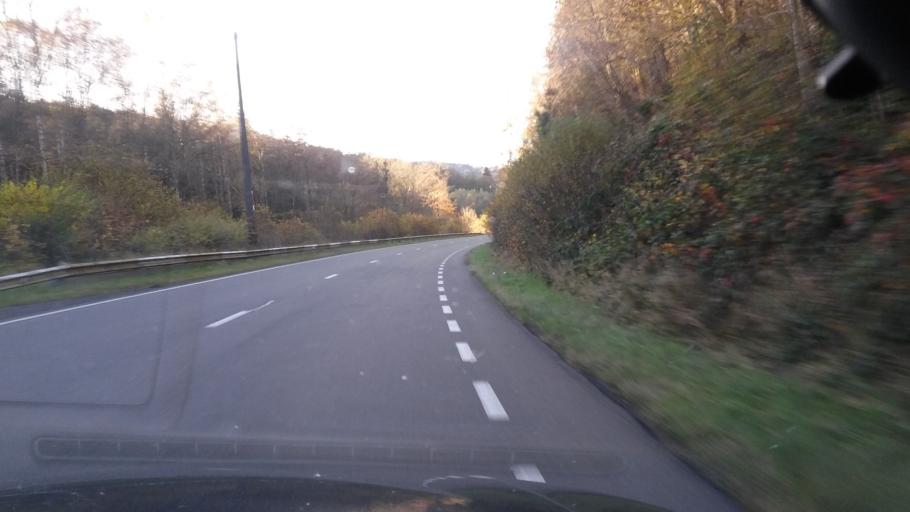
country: BE
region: Wallonia
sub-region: Province du Luxembourg
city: Bouillon
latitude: 49.7650
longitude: 5.0913
